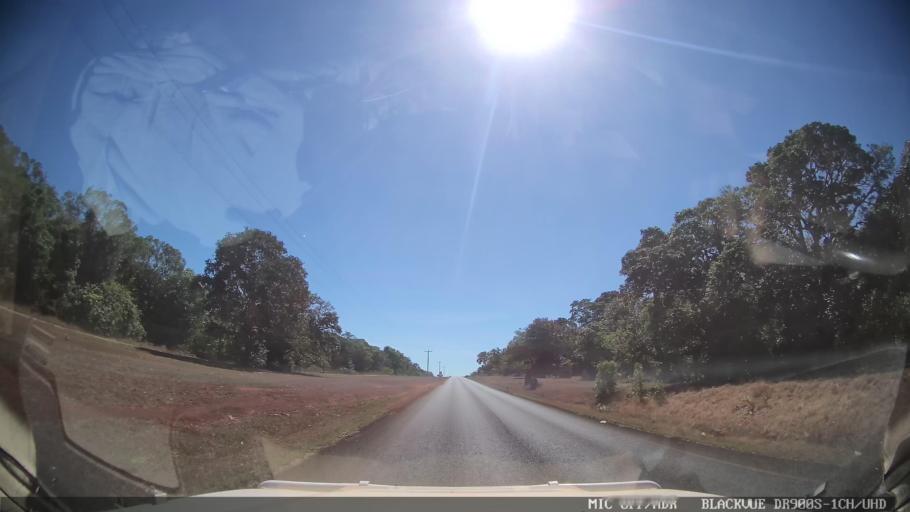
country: AU
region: Queensland
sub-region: Torres
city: Thursday Island
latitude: -10.9035
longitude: 142.3325
